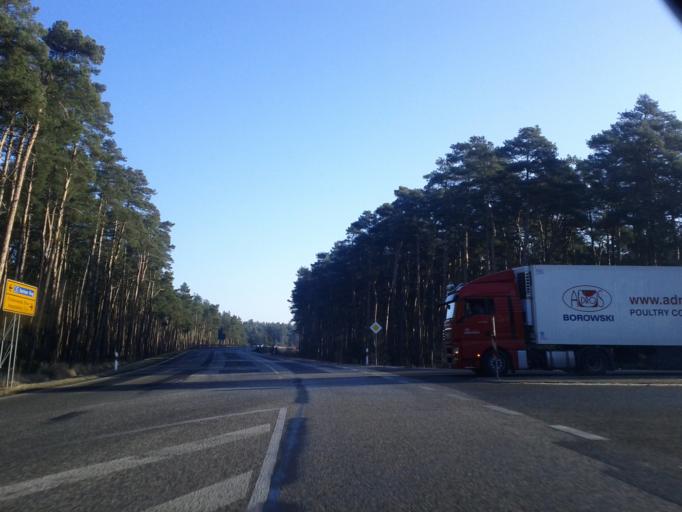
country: DE
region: Brandenburg
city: Grunheide
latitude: 52.3913
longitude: 13.7984
